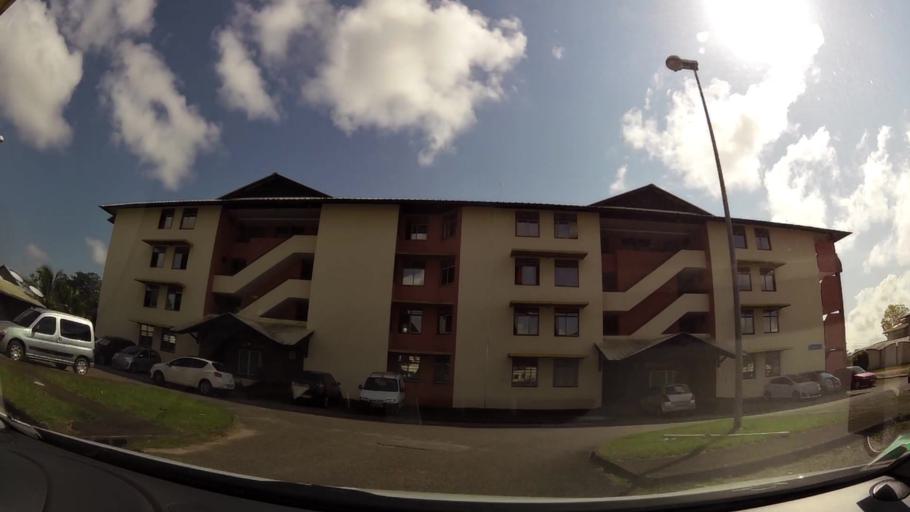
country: GF
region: Guyane
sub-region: Guyane
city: Cayenne
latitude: 4.9358
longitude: -52.3164
